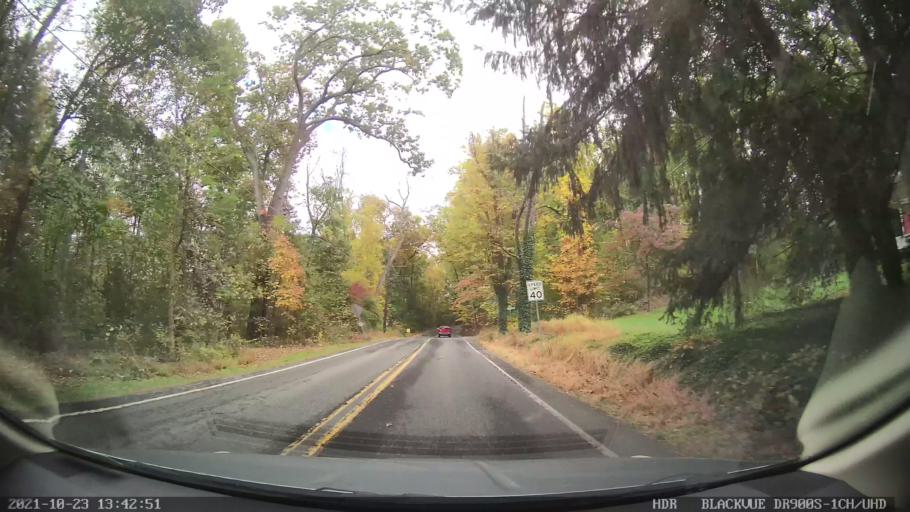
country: US
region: Pennsylvania
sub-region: Berks County
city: Bally
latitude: 40.4049
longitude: -75.5481
